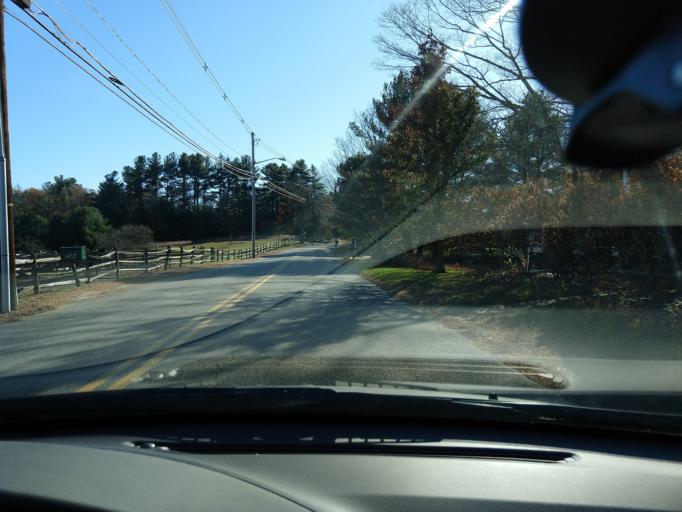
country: US
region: Massachusetts
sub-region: Middlesex County
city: Concord
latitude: 42.4947
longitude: -71.3330
